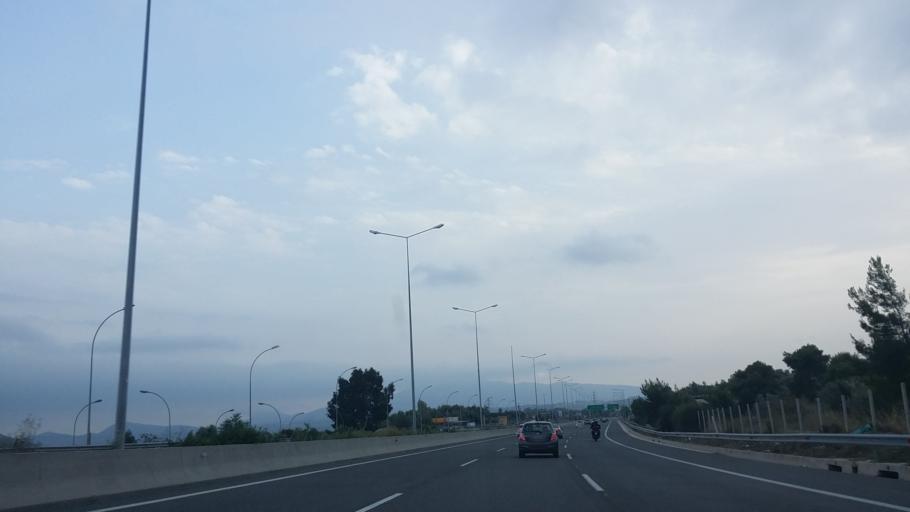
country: GR
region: Attica
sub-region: Nomarchia Anatolikis Attikis
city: Polydendri
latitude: 38.2111
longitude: 23.8551
